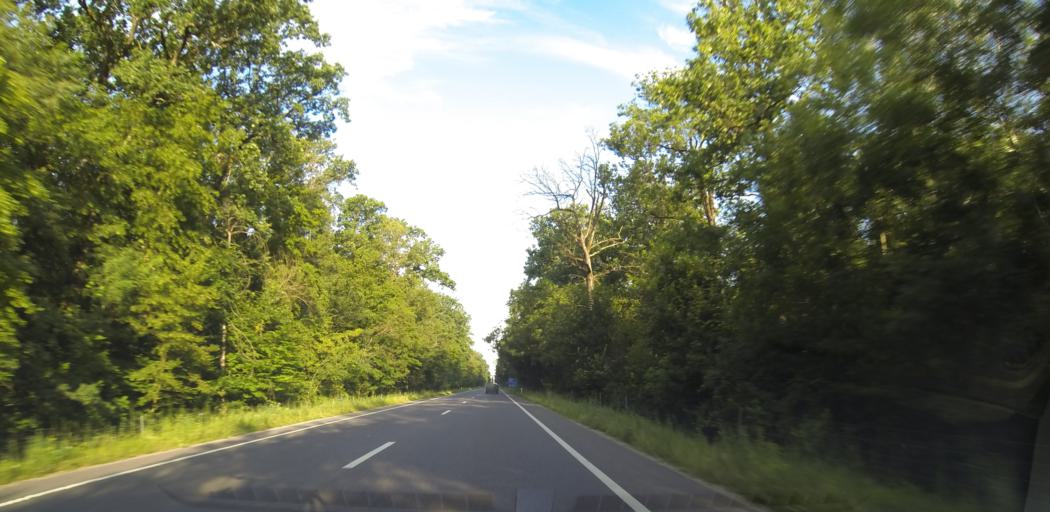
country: RO
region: Dolj
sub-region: Comuna Filiasi
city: Balta
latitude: 44.5697
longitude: 23.4457
